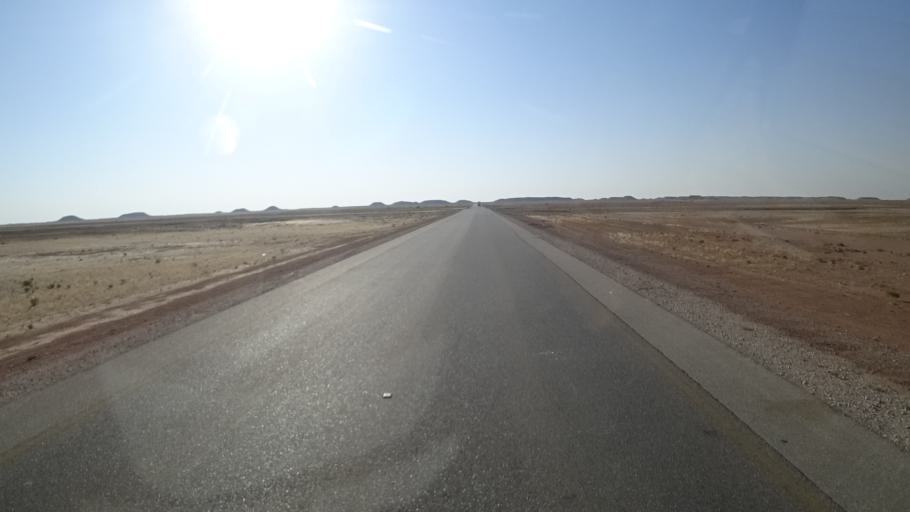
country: OM
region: Zufar
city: Salalah
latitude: 17.6418
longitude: 53.8288
